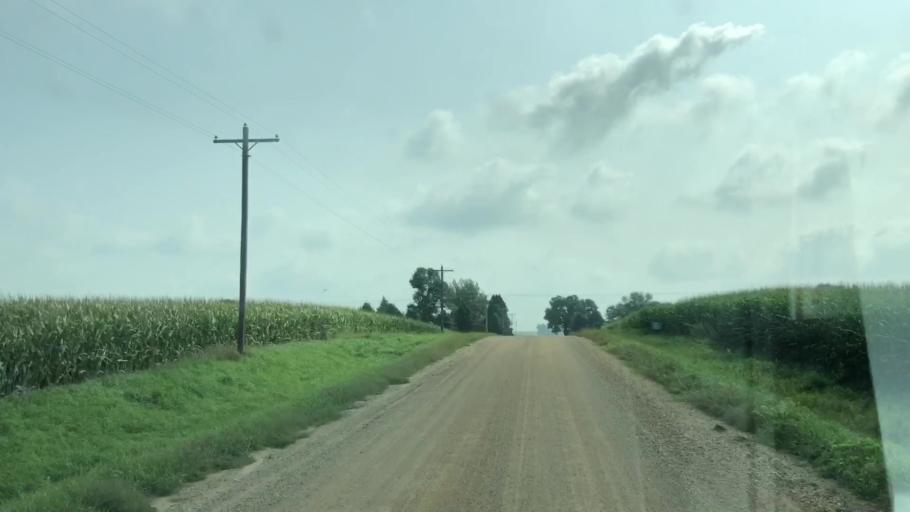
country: US
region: Iowa
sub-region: O'Brien County
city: Sheldon
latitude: 43.2152
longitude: -95.9637
